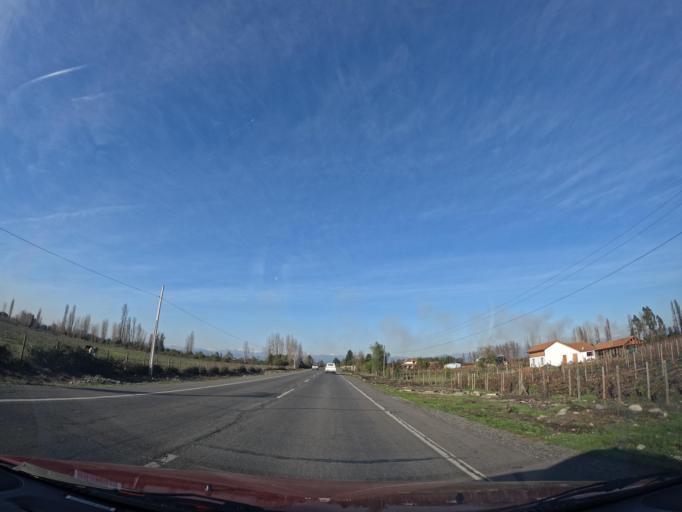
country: CL
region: Maule
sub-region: Provincia de Talca
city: San Clemente
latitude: -35.6273
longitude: -71.4720
